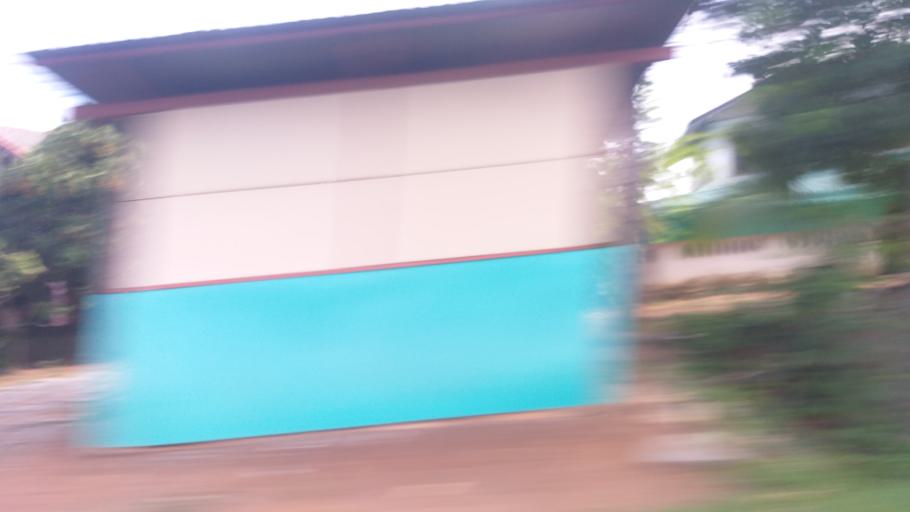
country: TH
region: Chaiyaphum
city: Ban Thaen
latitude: 16.3828
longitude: 102.3044
